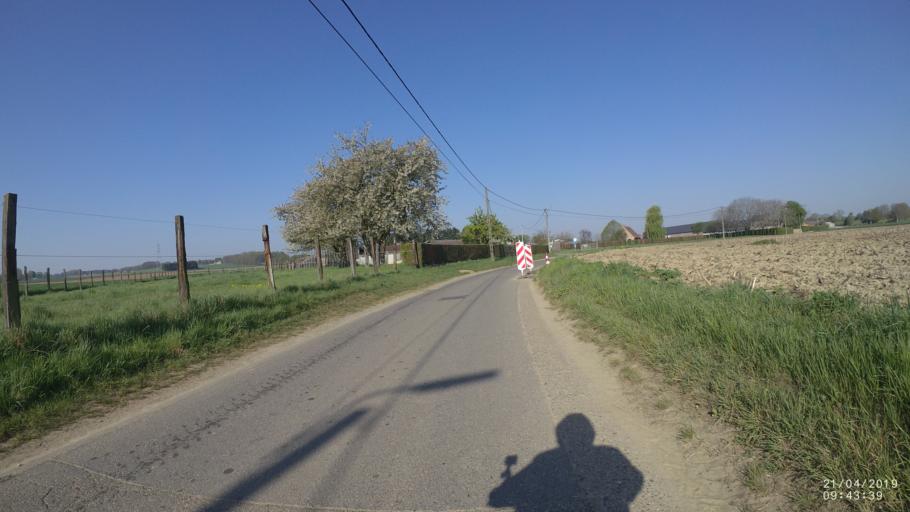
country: BE
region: Flanders
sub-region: Provincie Vlaams-Brabant
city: Holsbeek
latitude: 50.9150
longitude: 4.8039
